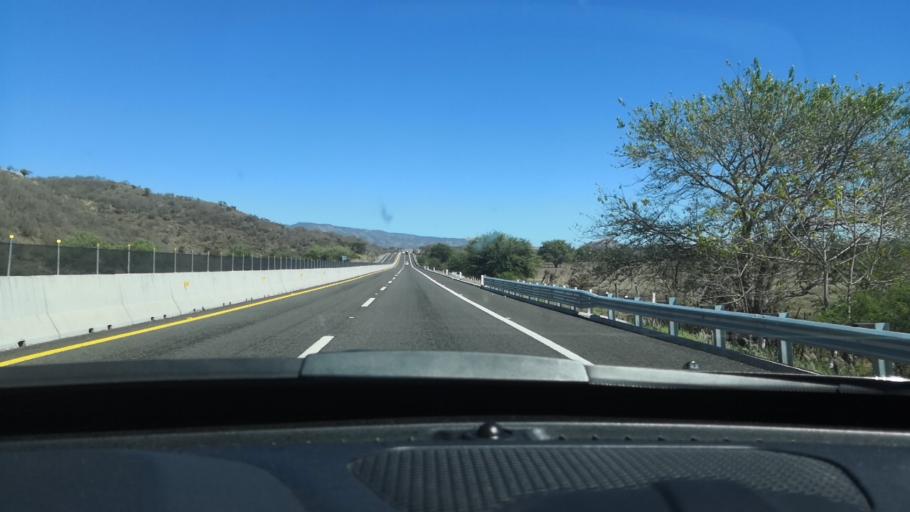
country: MX
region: Nayarit
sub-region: Ahuacatlan
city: Ahuacatlan
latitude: 21.0658
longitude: -104.4881
